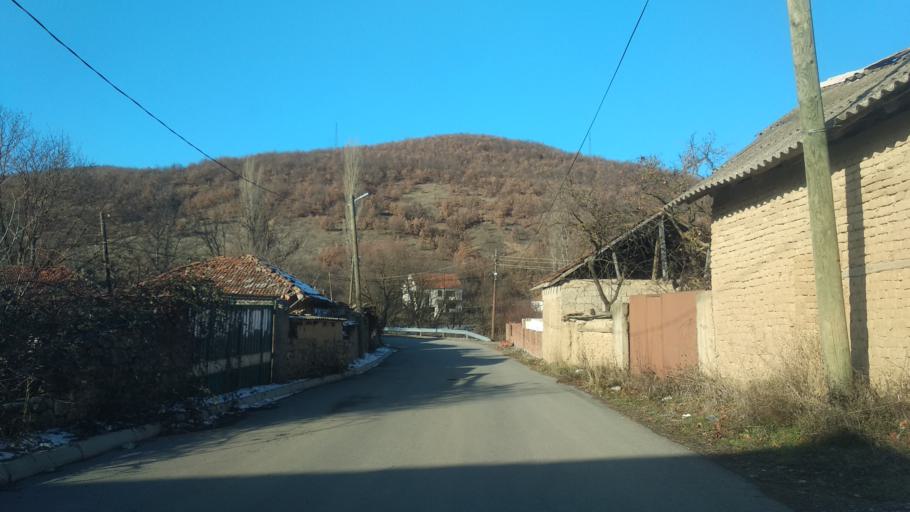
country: XK
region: Pristina
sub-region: Komuna e Prishtines
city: Pristina
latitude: 42.7146
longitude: 21.1692
